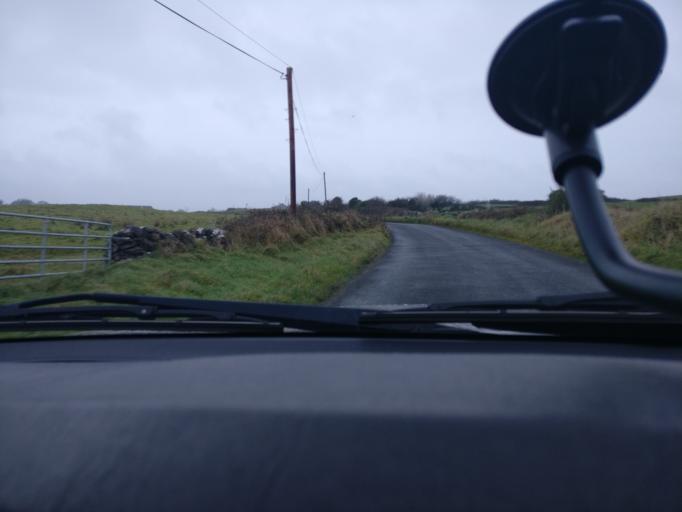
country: IE
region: Connaught
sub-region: County Galway
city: Loughrea
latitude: 53.2102
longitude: -8.5492
